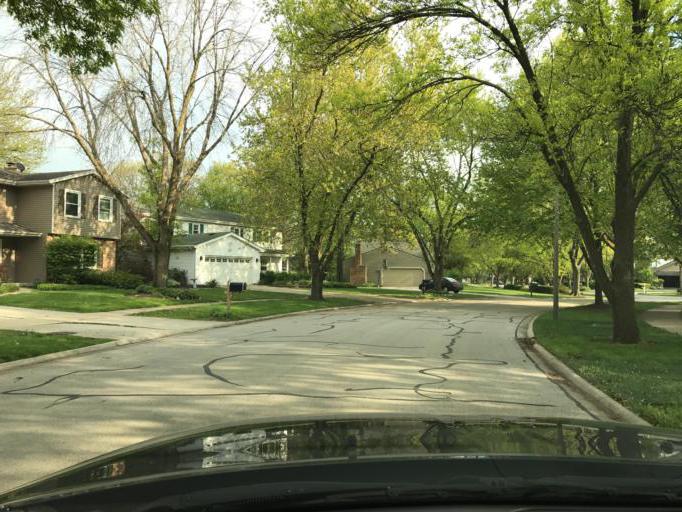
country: US
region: Illinois
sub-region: DuPage County
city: Naperville
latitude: 41.7599
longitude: -88.1164
